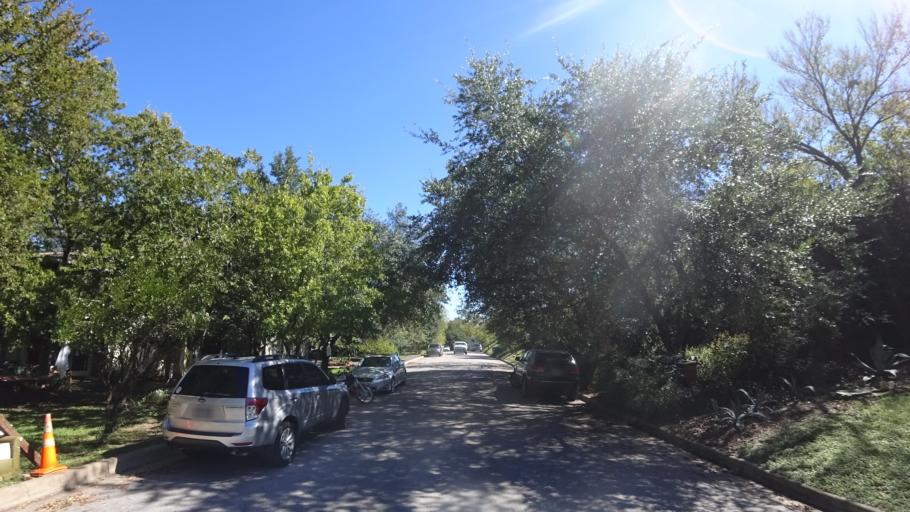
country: US
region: Texas
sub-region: Travis County
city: Austin
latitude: 30.2948
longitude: -97.7143
